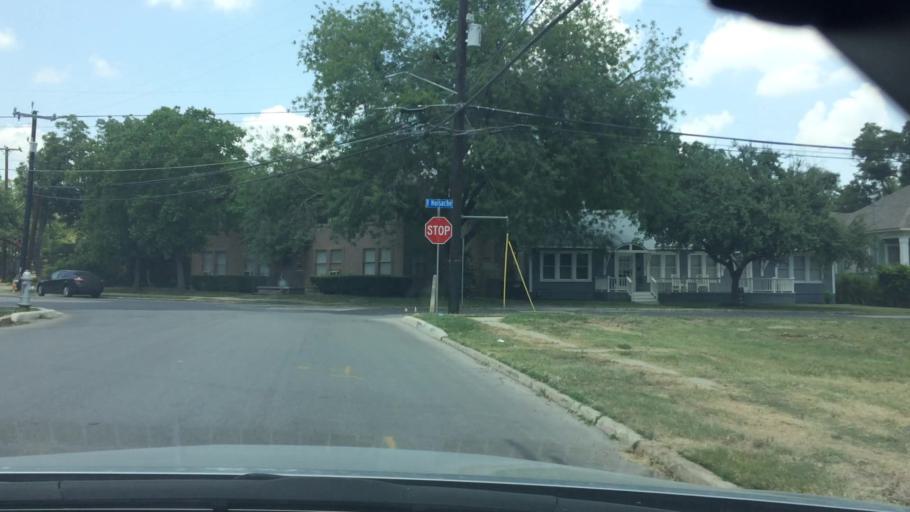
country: US
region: Texas
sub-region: Bexar County
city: Olmos Park
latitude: 29.4554
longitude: -98.4849
